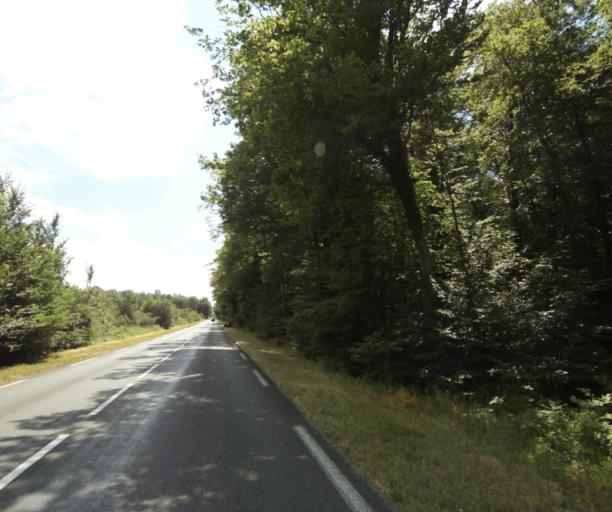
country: FR
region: Ile-de-France
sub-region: Departement de Seine-et-Marne
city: Bois-le-Roi
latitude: 48.4545
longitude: 2.7050
